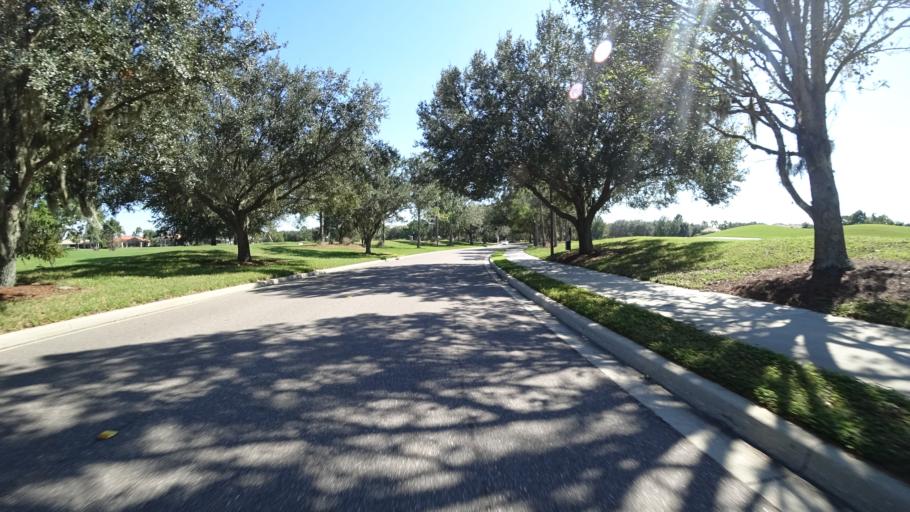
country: US
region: Florida
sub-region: Sarasota County
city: The Meadows
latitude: 27.3960
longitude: -82.4104
